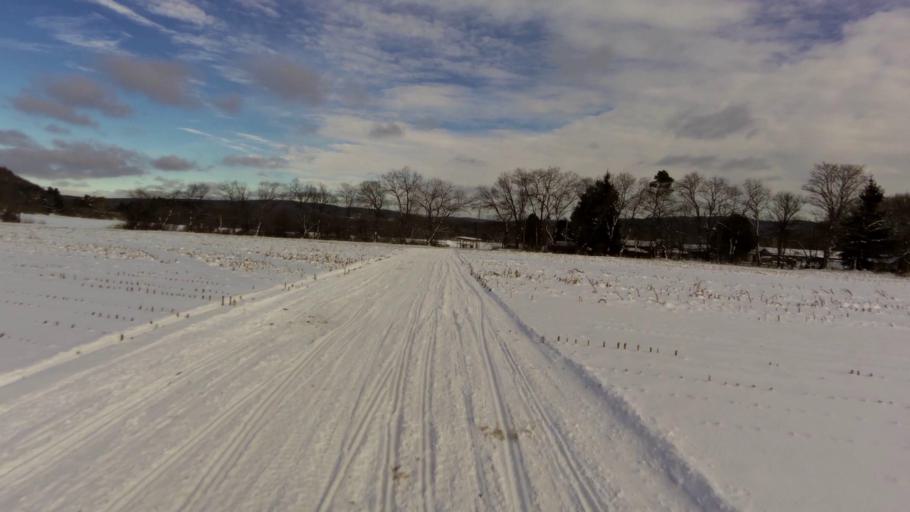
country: US
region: New York
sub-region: Cattaraugus County
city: Franklinville
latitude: 42.3387
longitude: -78.4692
